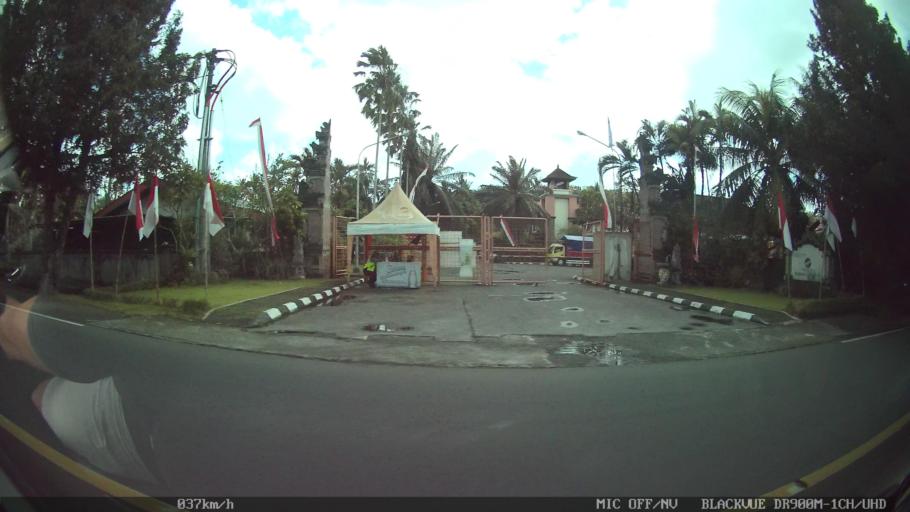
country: ID
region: Bali
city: Banjar Sedang
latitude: -8.5659
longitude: 115.2908
